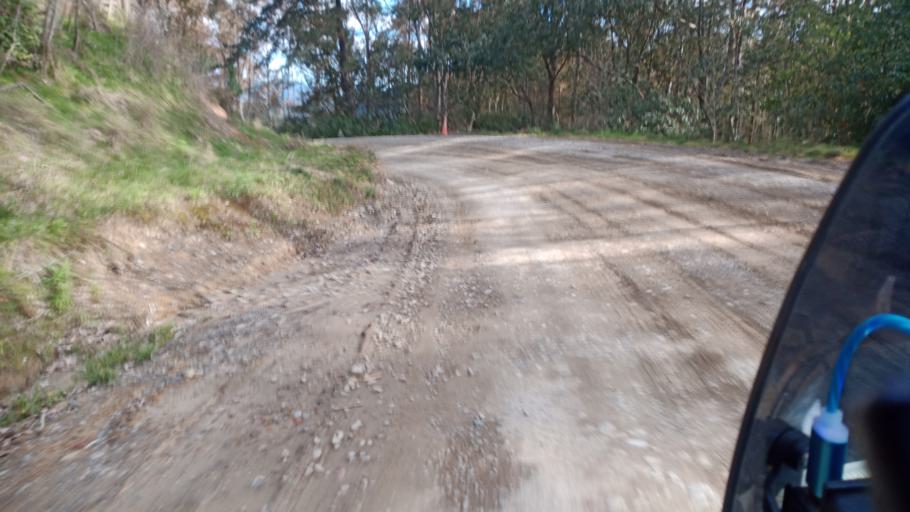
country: NZ
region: Gisborne
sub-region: Gisborne District
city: Gisborne
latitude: -38.1411
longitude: 178.1910
